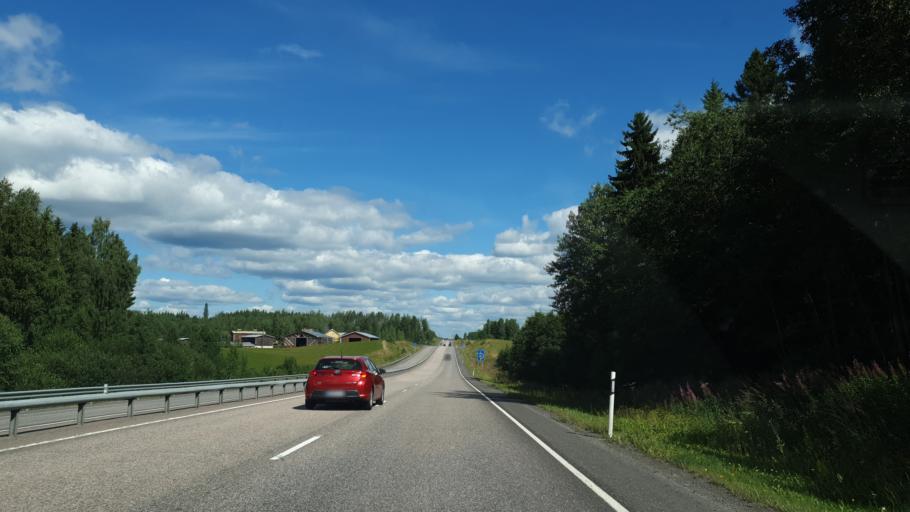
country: FI
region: Pirkanmaa
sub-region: Tampere
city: Orivesi
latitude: 61.6952
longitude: 24.4210
